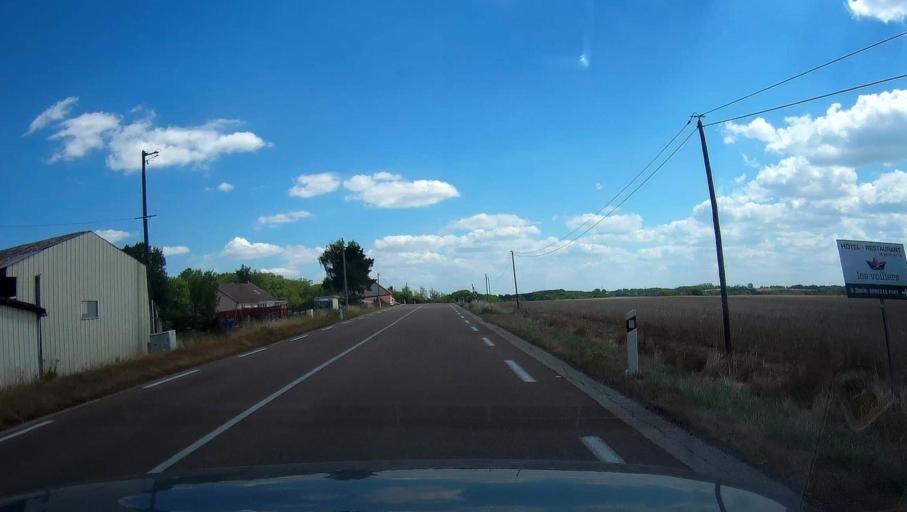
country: FR
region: Champagne-Ardenne
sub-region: Departement de la Haute-Marne
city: Langres
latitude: 47.8561
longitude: 5.3518
